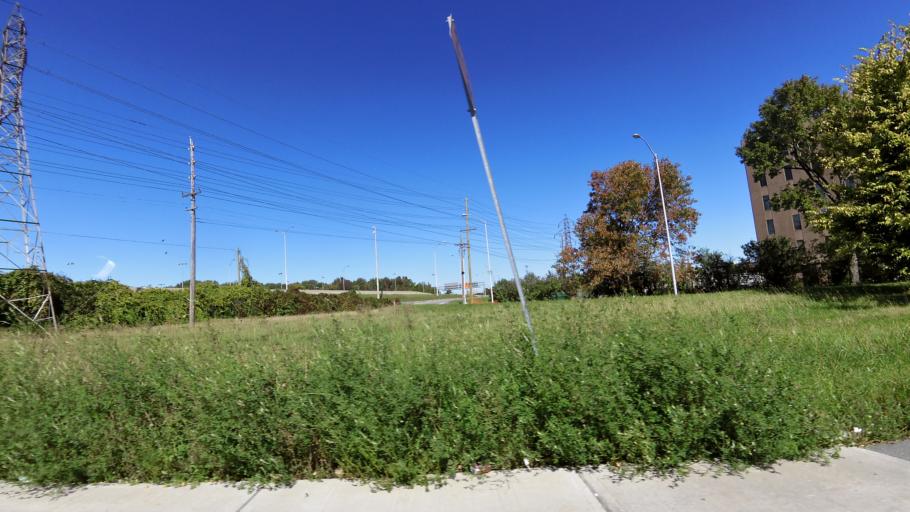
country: CA
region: Ontario
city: Ottawa
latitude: 45.3853
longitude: -75.7368
